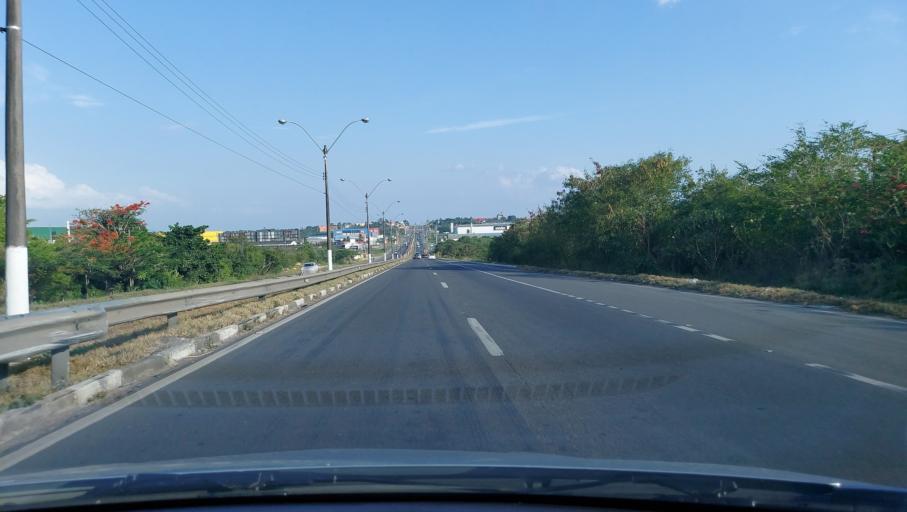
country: BR
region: Bahia
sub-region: Feira De Santana
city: Feira de Santana
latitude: -12.2836
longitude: -38.9204
